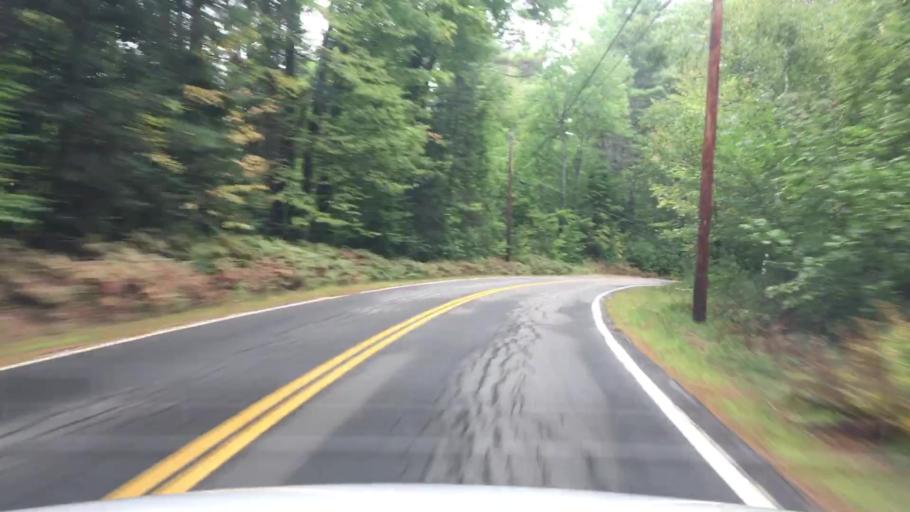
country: US
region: New Hampshire
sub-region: Carroll County
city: Effingham
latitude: 43.7437
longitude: -71.0066
